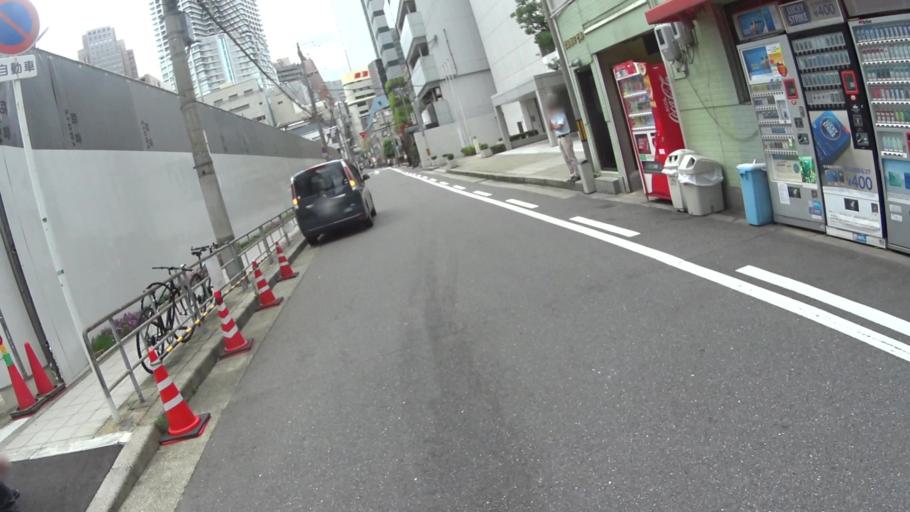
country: JP
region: Osaka
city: Osaka-shi
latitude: 34.6957
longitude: 135.4940
